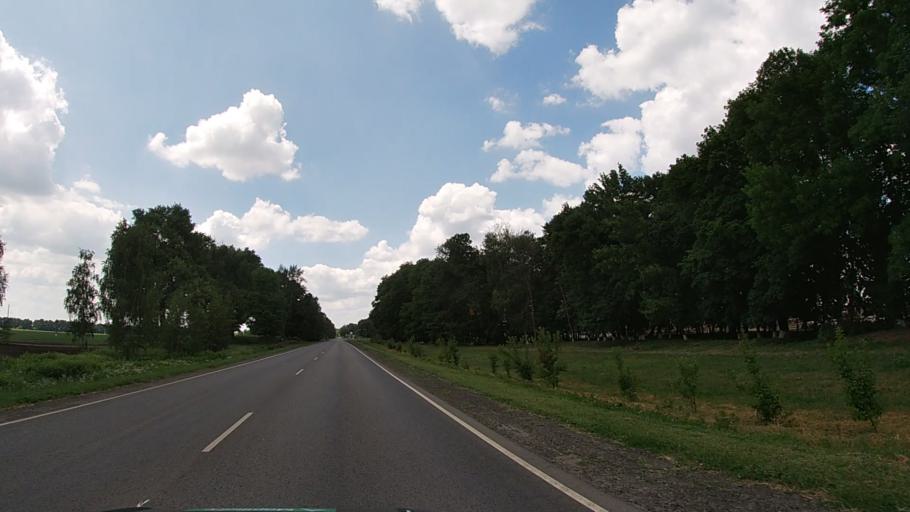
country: RU
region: Belgorod
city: Grayvoron
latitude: 50.4949
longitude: 35.7101
